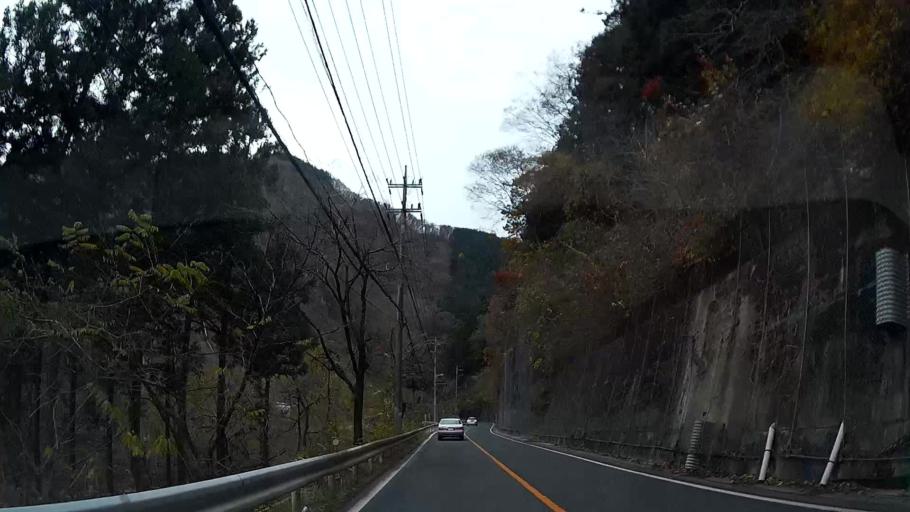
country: JP
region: Saitama
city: Chichibu
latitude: 35.9386
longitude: 138.9637
